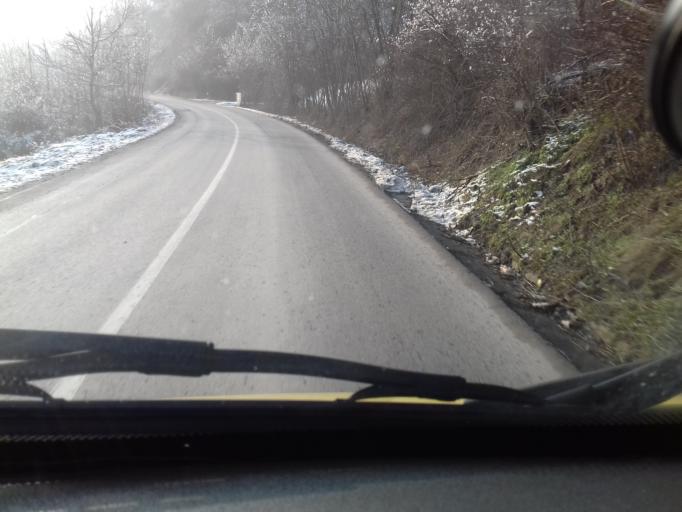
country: BA
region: Federation of Bosnia and Herzegovina
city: Visoko
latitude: 43.9985
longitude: 18.2119
